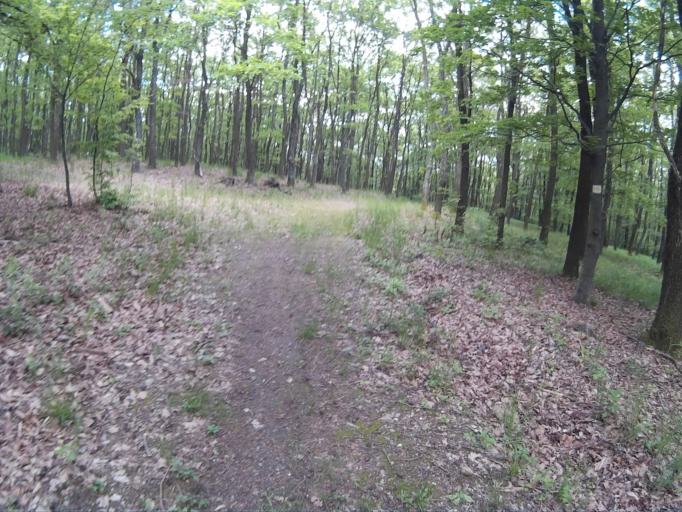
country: HU
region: Vas
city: Koszeg
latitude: 47.3743
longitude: 16.5025
